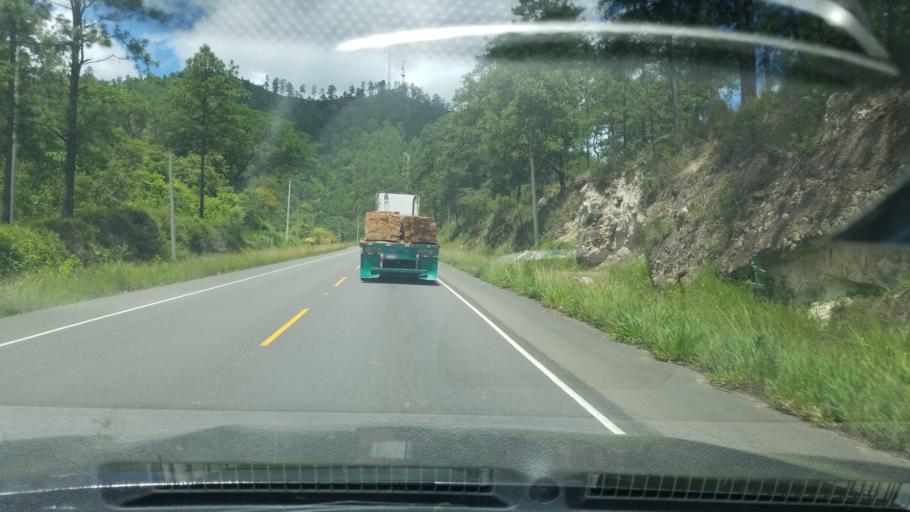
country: HN
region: Francisco Morazan
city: Talanga
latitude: 14.3949
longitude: -87.1282
